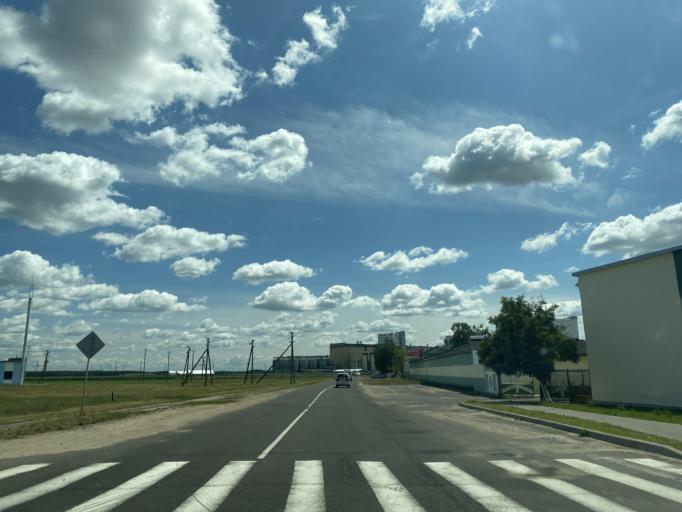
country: BY
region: Brest
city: Ivanava
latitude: 52.1415
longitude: 25.5483
